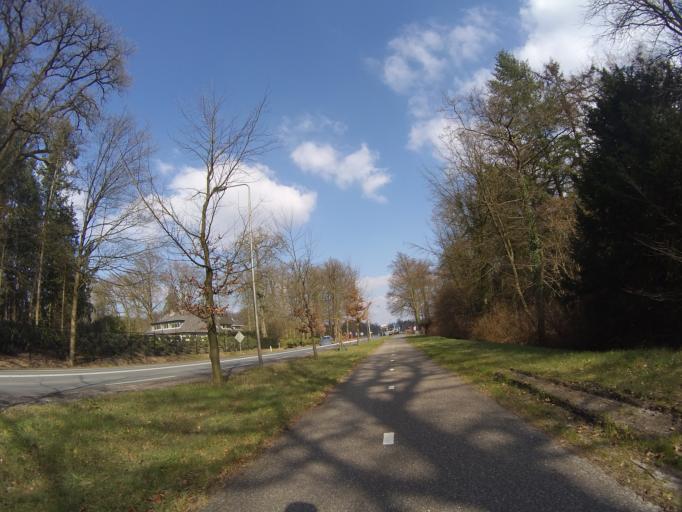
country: NL
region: Utrecht
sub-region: Gemeente Soest
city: Soest
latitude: 52.1649
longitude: 5.2379
